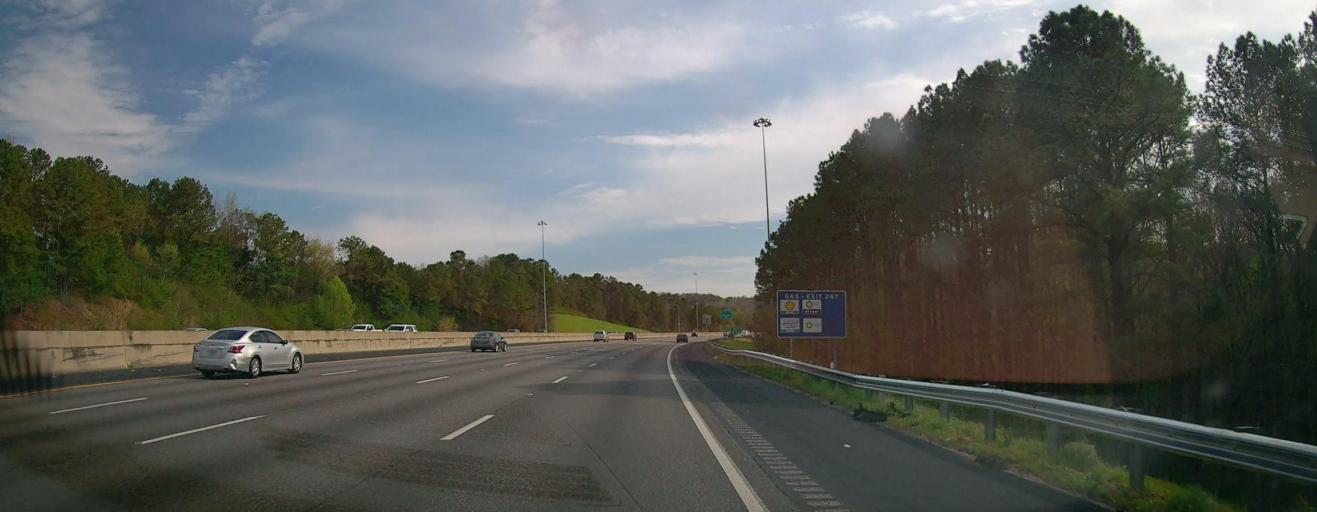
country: US
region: Alabama
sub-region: Shelby County
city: Indian Springs Village
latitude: 33.3664
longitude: -86.7769
